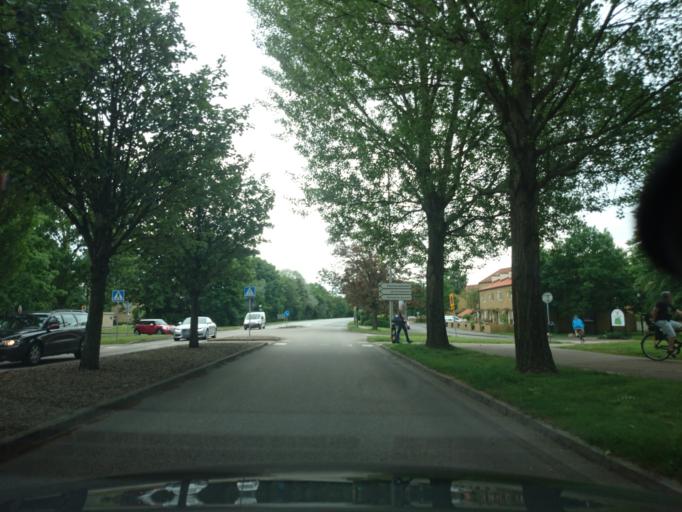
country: SE
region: Skane
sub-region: Landskrona
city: Landskrona
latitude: 55.8860
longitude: 12.8313
